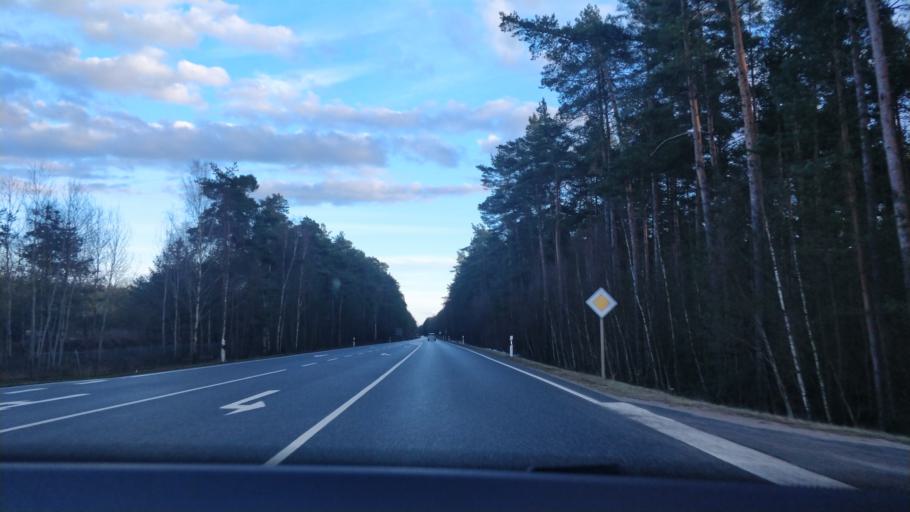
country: DE
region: Bavaria
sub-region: Upper Palatinate
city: Pressath
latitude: 49.7379
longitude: 11.9503
